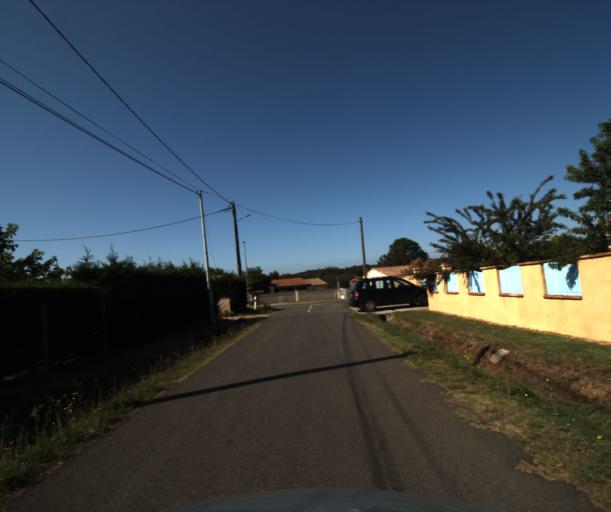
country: FR
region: Midi-Pyrenees
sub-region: Departement de la Haute-Garonne
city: Eaunes
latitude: 43.4309
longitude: 1.3502
